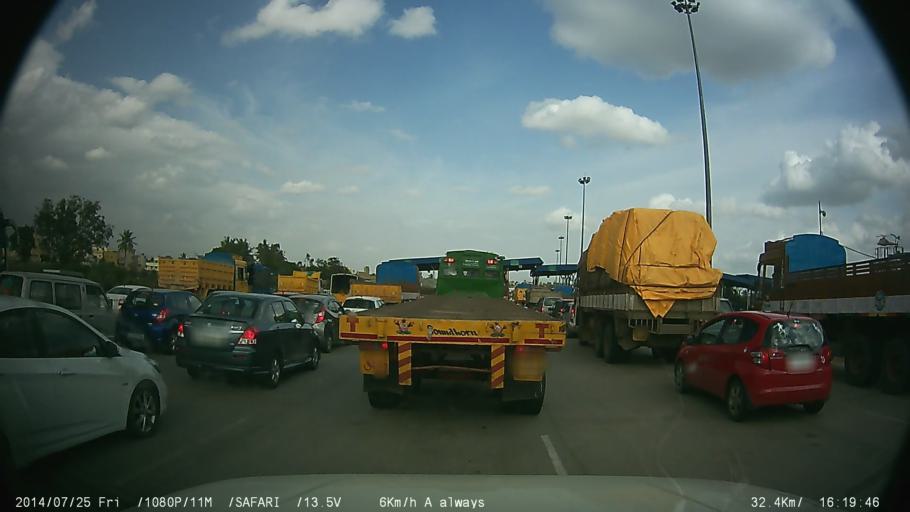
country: IN
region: Tamil Nadu
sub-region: Krishnagiri
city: Hosur
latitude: 12.7773
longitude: 77.7765
